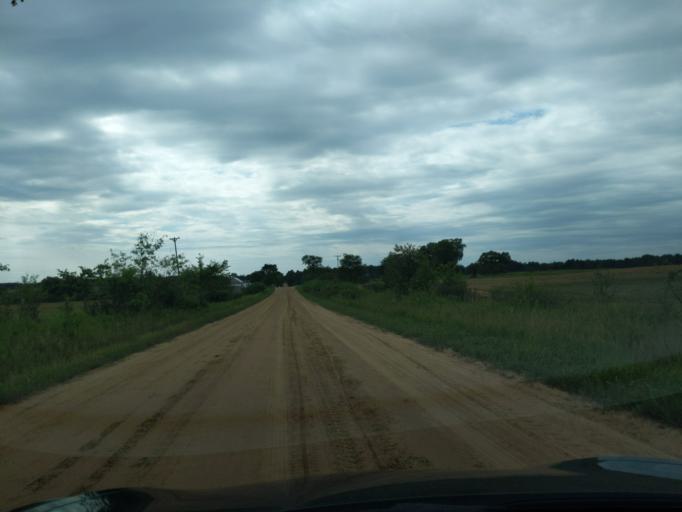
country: US
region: Michigan
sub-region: Clare County
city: Harrison
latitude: 44.0024
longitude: -84.9942
